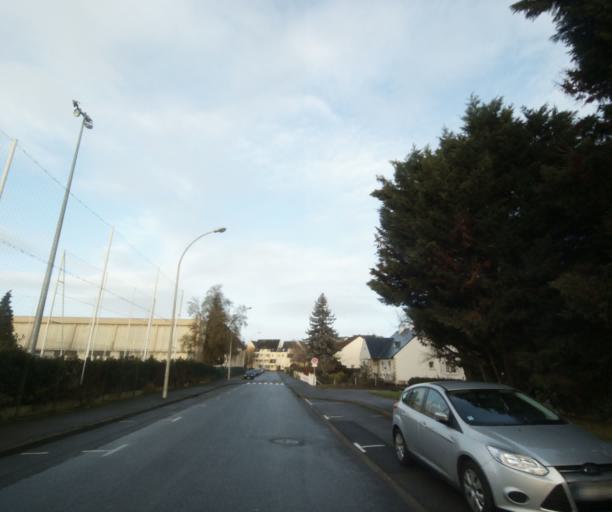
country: FR
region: Pays de la Loire
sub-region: Departement de la Sarthe
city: Le Mans
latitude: 47.9720
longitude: 0.2239
